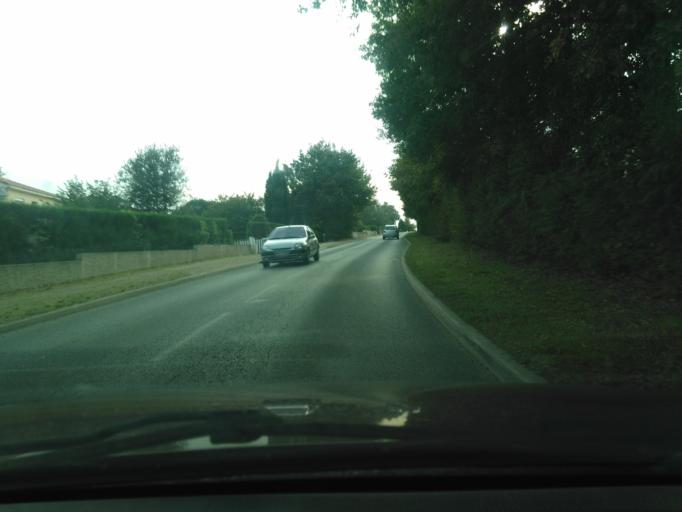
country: FR
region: Pays de la Loire
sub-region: Departement de la Vendee
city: Dompierre-sur-Yon
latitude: 46.7256
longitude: -1.3975
